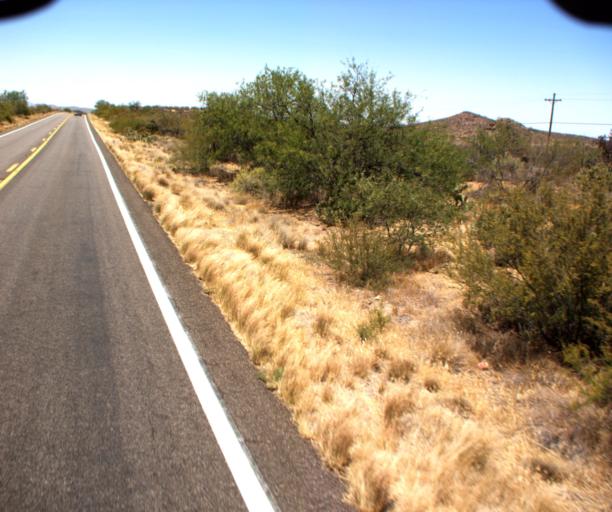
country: US
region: Arizona
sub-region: Pima County
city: Catalina
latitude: 32.6477
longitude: -111.0252
